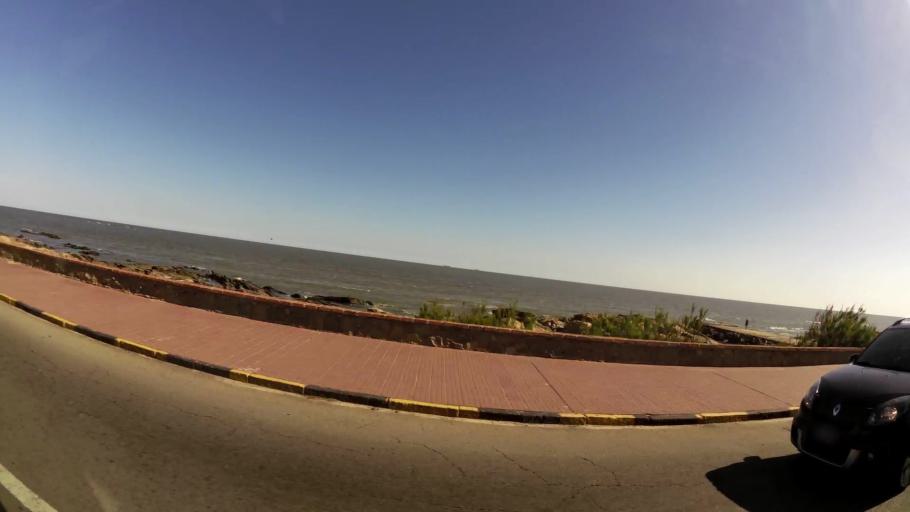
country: UY
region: Canelones
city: Paso de Carrasco
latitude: -34.8993
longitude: -56.0655
